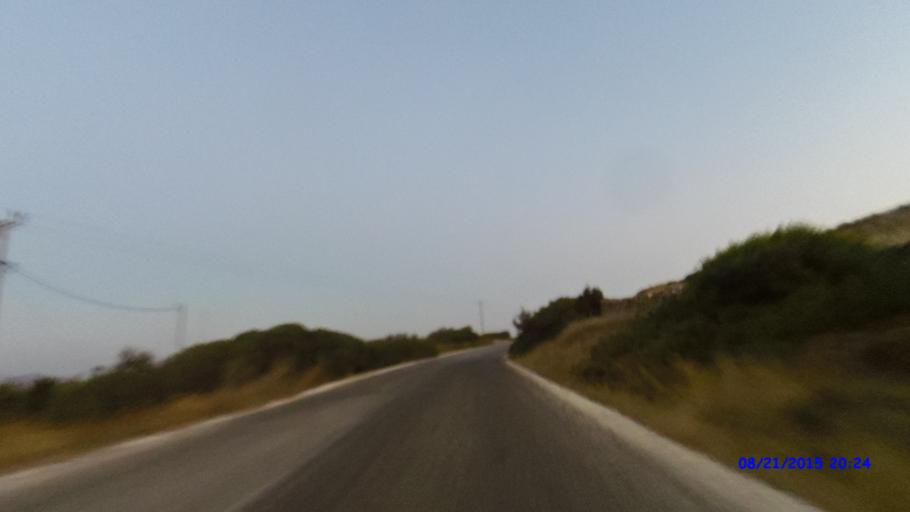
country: GR
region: South Aegean
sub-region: Nomos Kykladon
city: Antiparos
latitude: 36.9913
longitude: 25.0713
